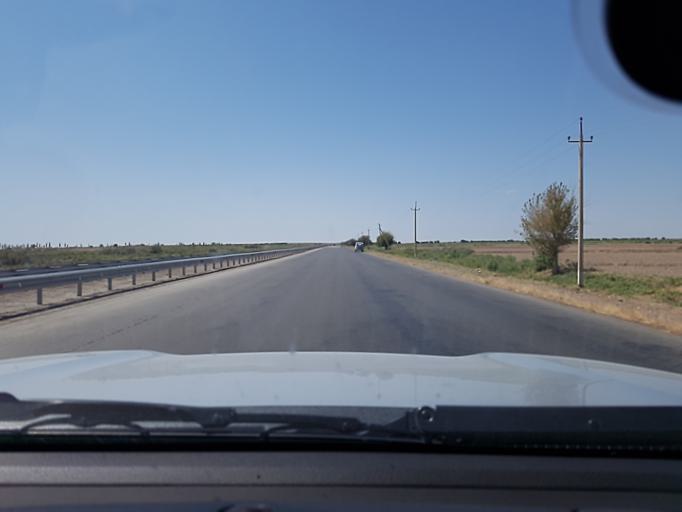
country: TM
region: Dasoguz
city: Yylanly
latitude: 41.7571
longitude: 59.4080
